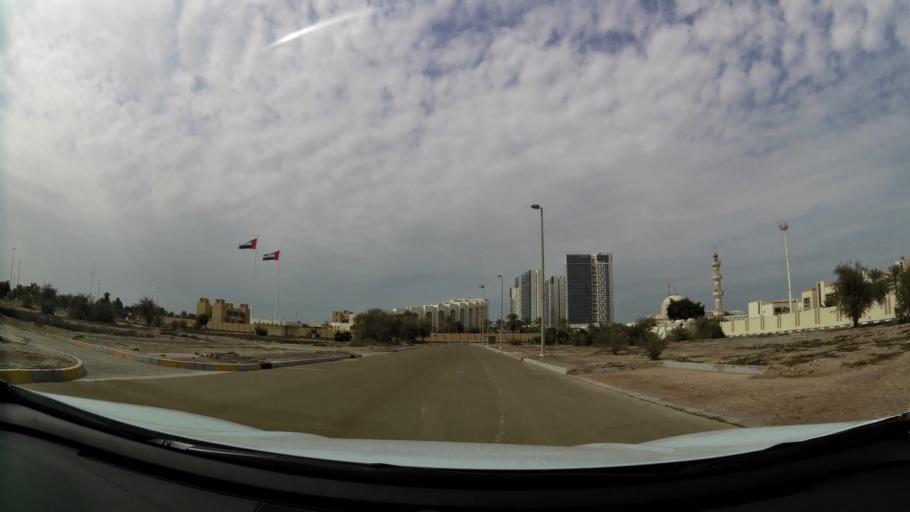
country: AE
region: Abu Dhabi
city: Abu Dhabi
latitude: 24.4109
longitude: 54.4689
